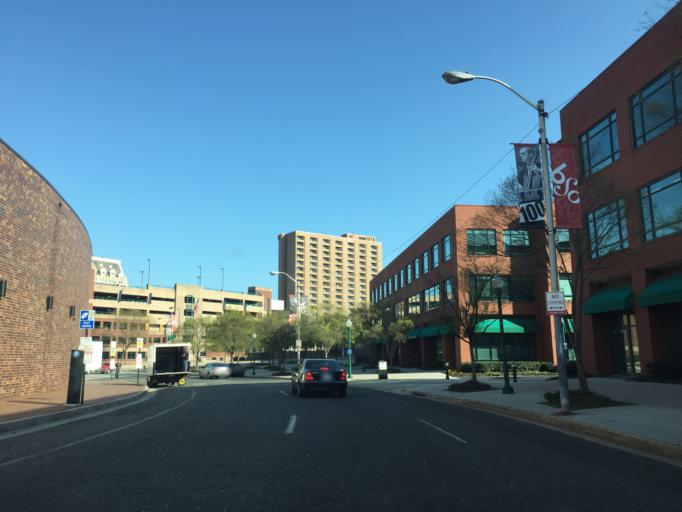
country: US
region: Maryland
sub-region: City of Baltimore
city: Baltimore
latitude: 39.3038
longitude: -76.6194
